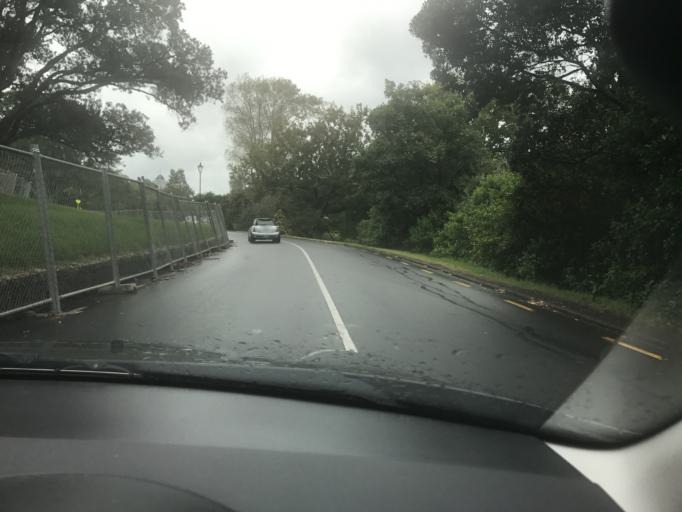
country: NZ
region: Auckland
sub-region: Auckland
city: Auckland
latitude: -36.8586
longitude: 174.7784
